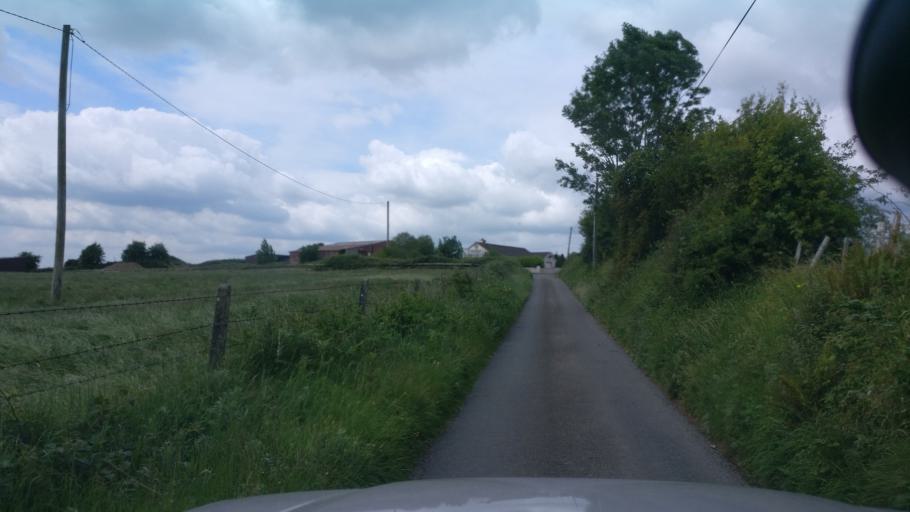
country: IE
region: Connaught
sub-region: County Galway
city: Ballinasloe
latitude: 53.2874
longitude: -8.3166
